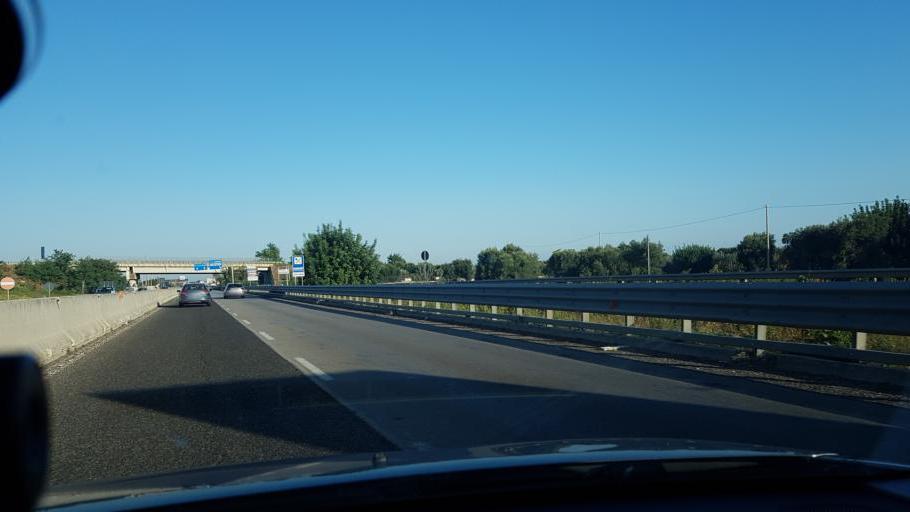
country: IT
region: Apulia
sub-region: Provincia di Brindisi
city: Fasano
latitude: 40.8492
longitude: 17.3594
